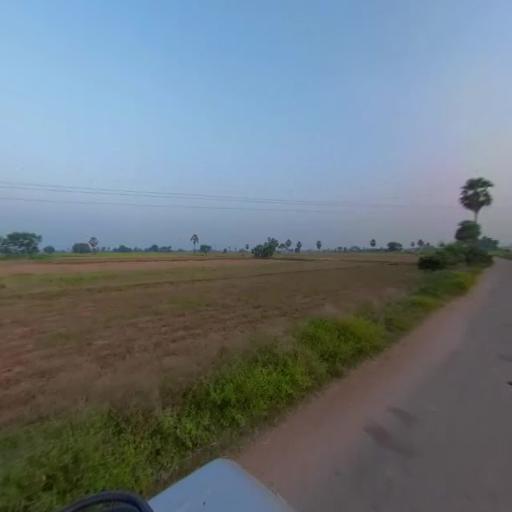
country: IN
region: Telangana
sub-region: Nalgonda
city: Suriapet
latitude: 17.0782
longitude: 79.5496
